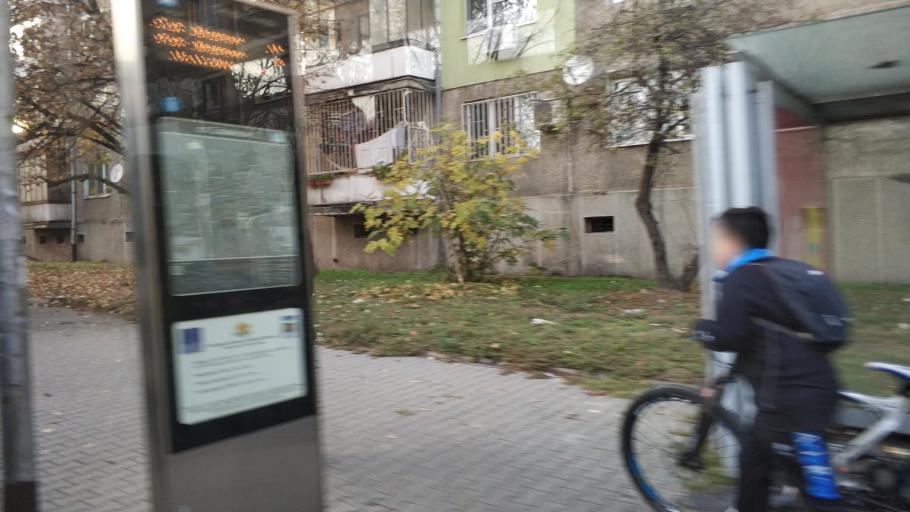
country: BG
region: Stara Zagora
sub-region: Obshtina Stara Zagora
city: Stara Zagora
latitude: 42.4186
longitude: 25.6226
